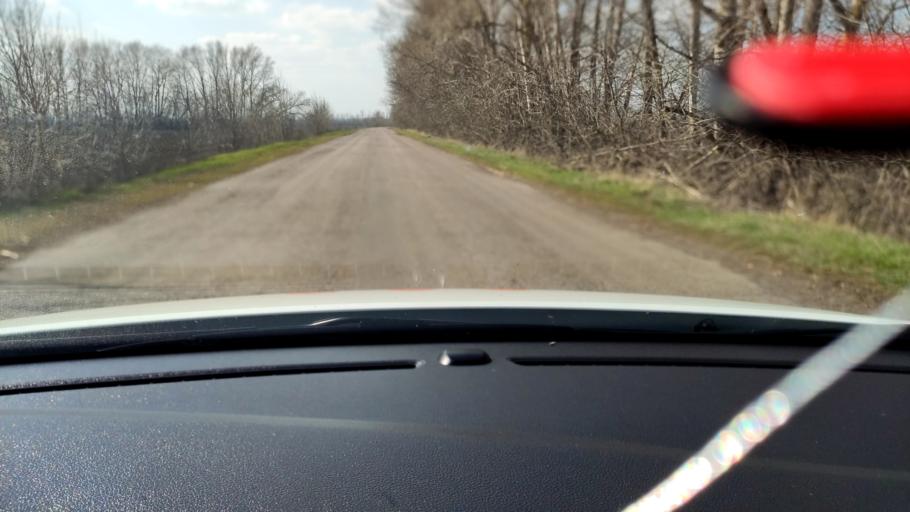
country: RU
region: Voronezj
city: Uryv-Pokrovka
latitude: 51.1302
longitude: 39.1026
